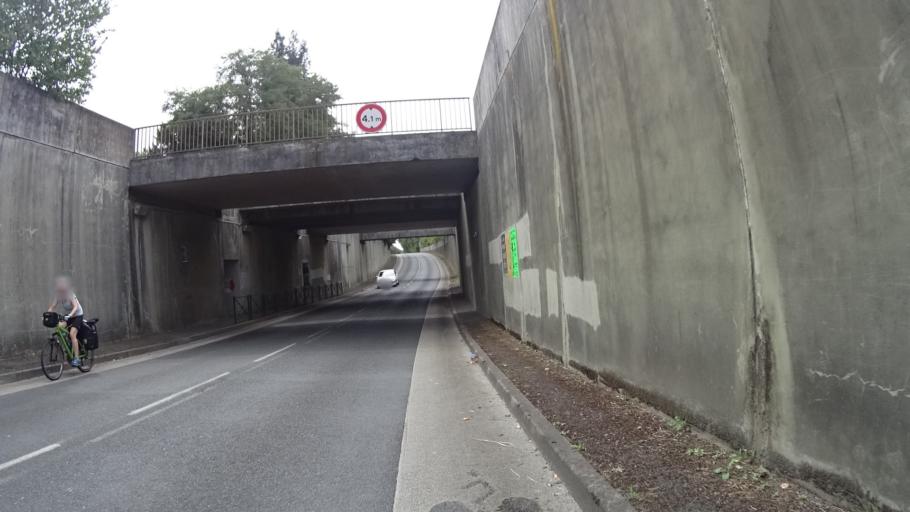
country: FR
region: Pays de la Loire
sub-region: Departement de Maine-et-Loire
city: Savennieres
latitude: 47.3815
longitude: -0.6556
